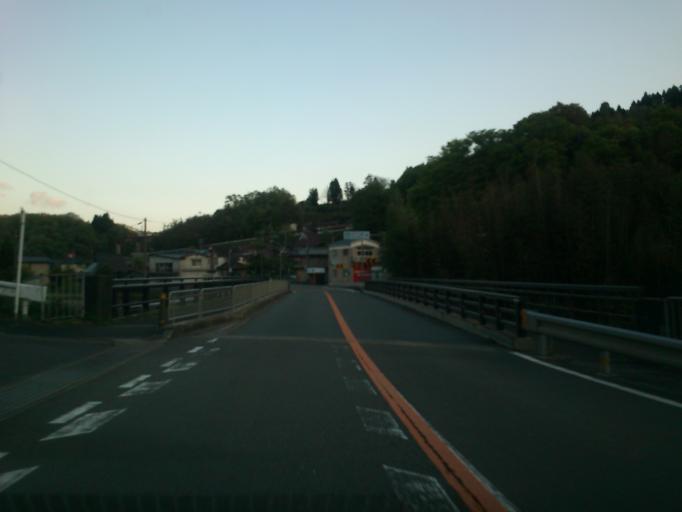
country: JP
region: Kyoto
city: Ayabe
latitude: 35.2130
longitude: 135.4249
